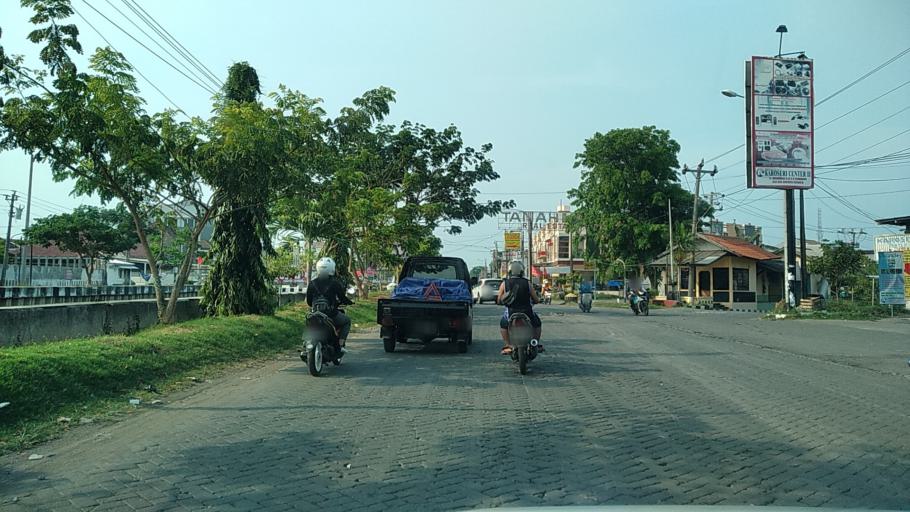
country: ID
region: Central Java
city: Semarang
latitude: -6.9636
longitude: 110.4110
